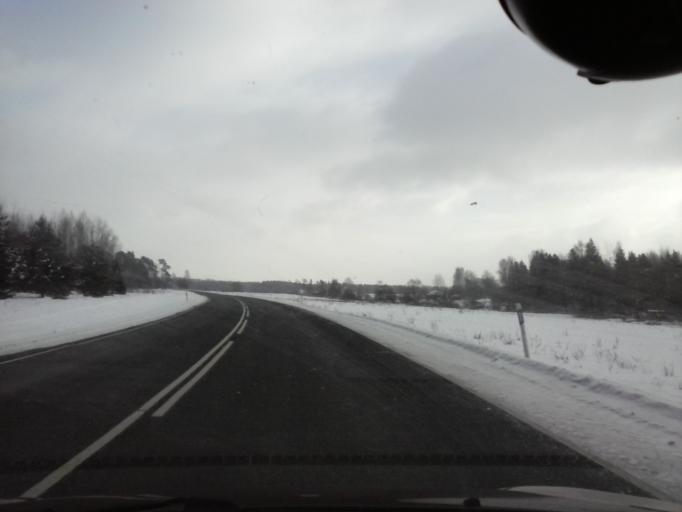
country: EE
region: Viljandimaa
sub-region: Viljandi linn
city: Viljandi
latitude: 58.3440
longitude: 25.4656
